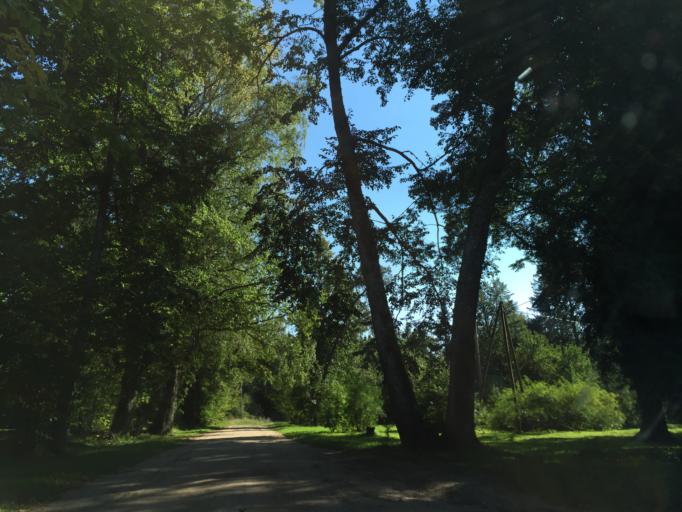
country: LV
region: Limbazu Rajons
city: Limbazi
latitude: 57.5511
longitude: 24.7706
